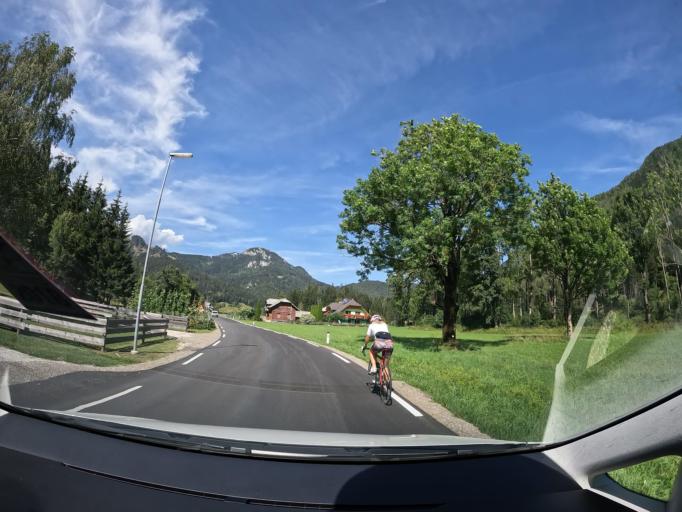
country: AT
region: Carinthia
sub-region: Politischer Bezirk Feldkirchen
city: Feldkirchen in Karnten
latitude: 46.6920
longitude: 14.1228
